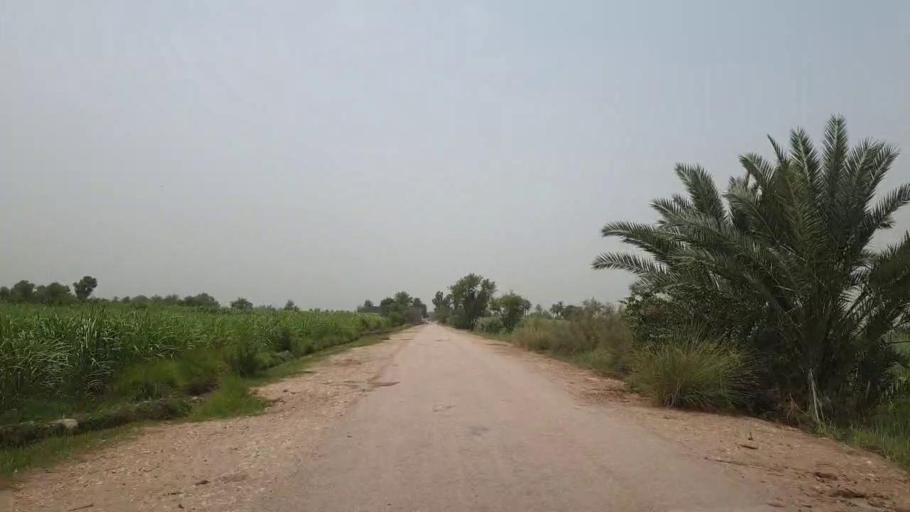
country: PK
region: Sindh
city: Sobhadero
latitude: 27.4213
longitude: 68.4235
